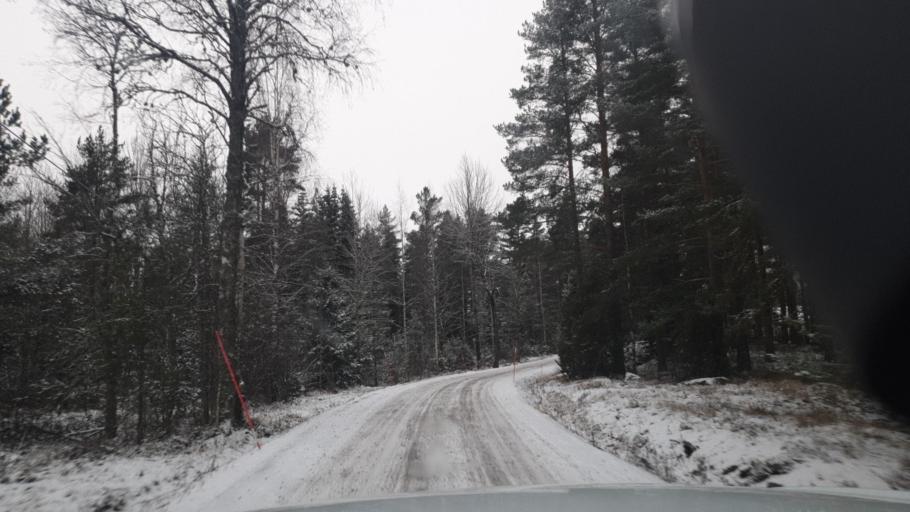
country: SE
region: Vaermland
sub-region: Karlstads Kommun
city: Edsvalla
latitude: 59.6215
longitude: 13.0640
